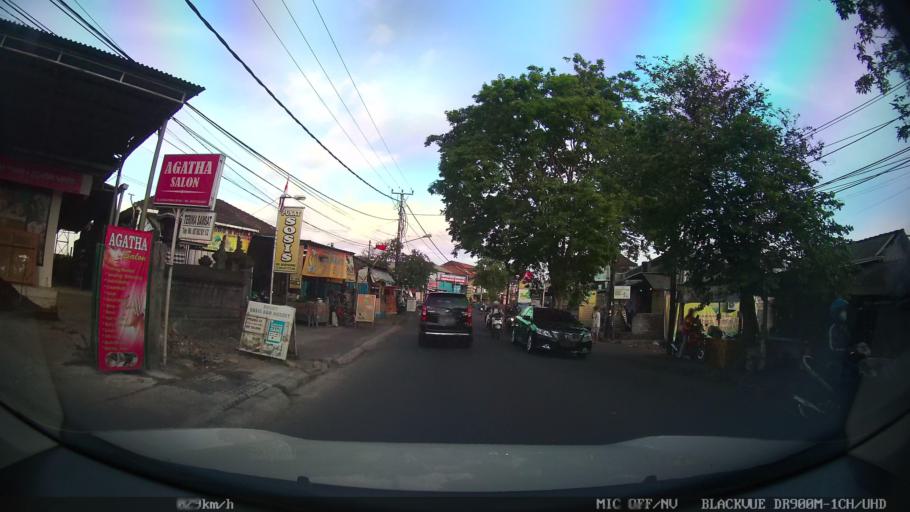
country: ID
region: Bali
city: Banjar Kertasari
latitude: -8.6301
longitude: 115.2093
